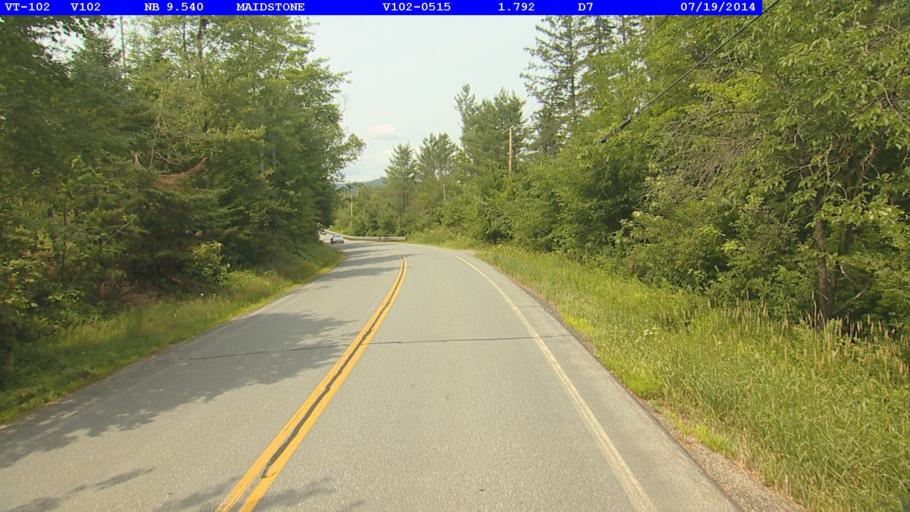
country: US
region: Vermont
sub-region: Essex County
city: Guildhall
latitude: 44.5927
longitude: -71.5530
